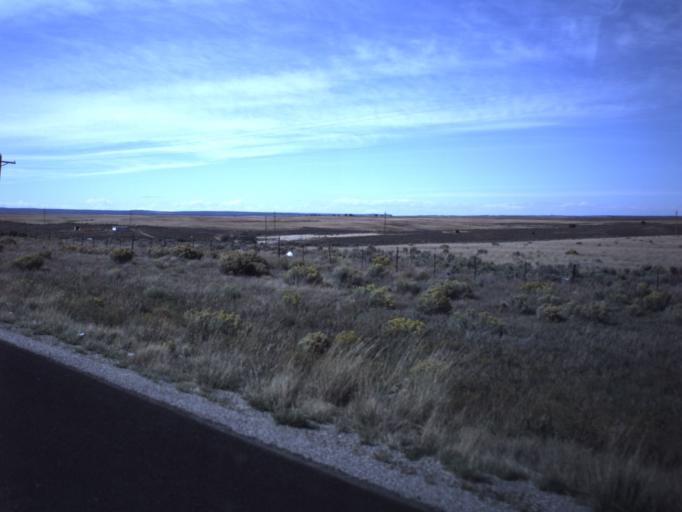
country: US
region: Utah
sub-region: San Juan County
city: Monticello
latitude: 37.8684
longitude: -109.2438
